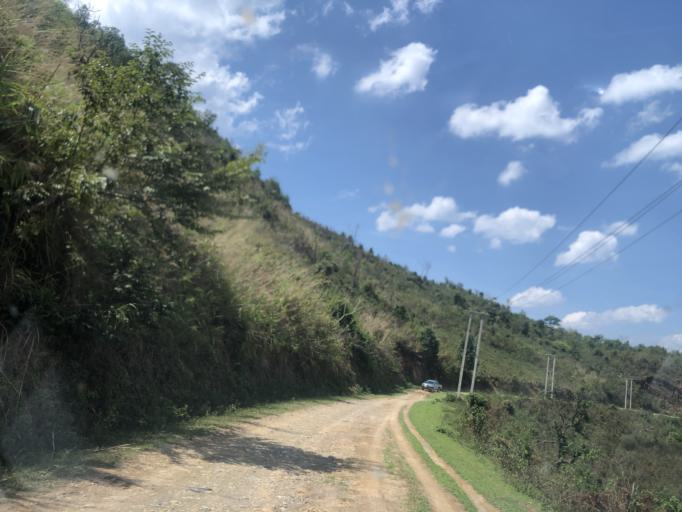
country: LA
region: Phongsali
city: Phongsali
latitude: 21.4092
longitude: 102.2397
